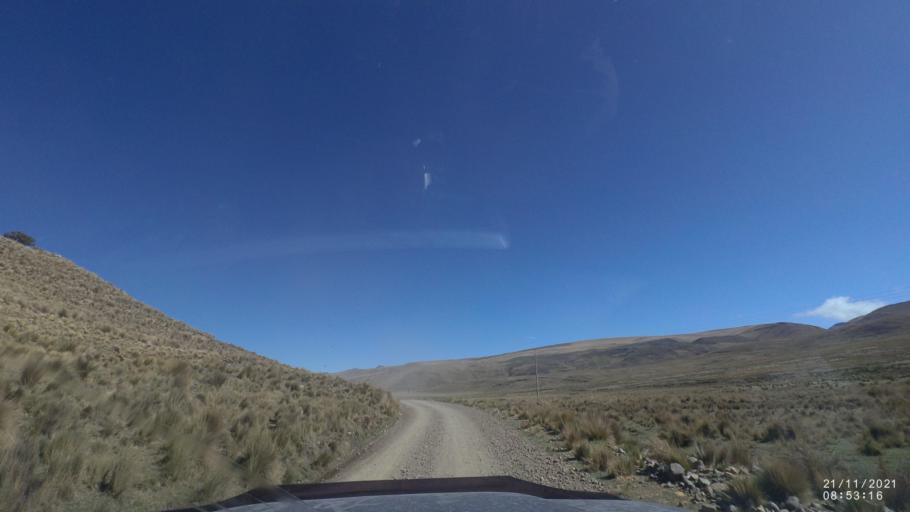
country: BO
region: Cochabamba
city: Cochabamba
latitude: -17.2095
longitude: -66.2411
